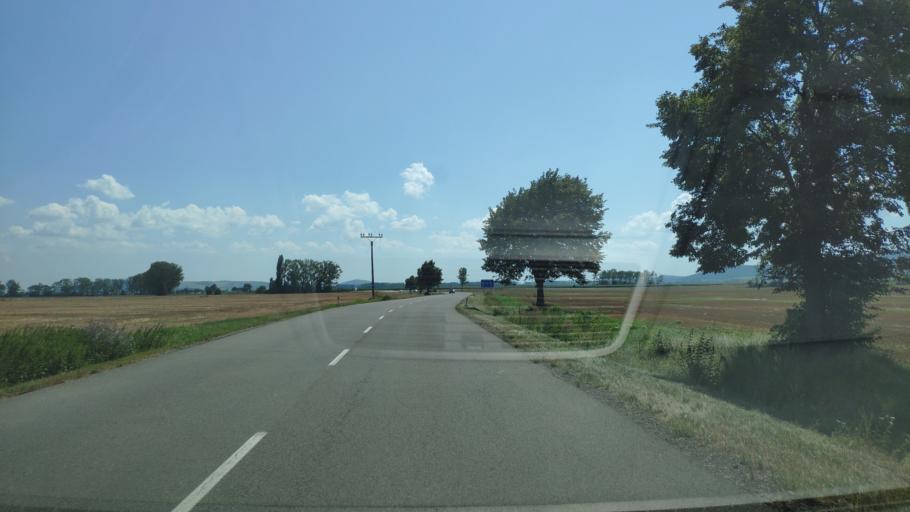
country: SK
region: Kosicky
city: Trebisov
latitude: 48.5515
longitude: 21.6845
